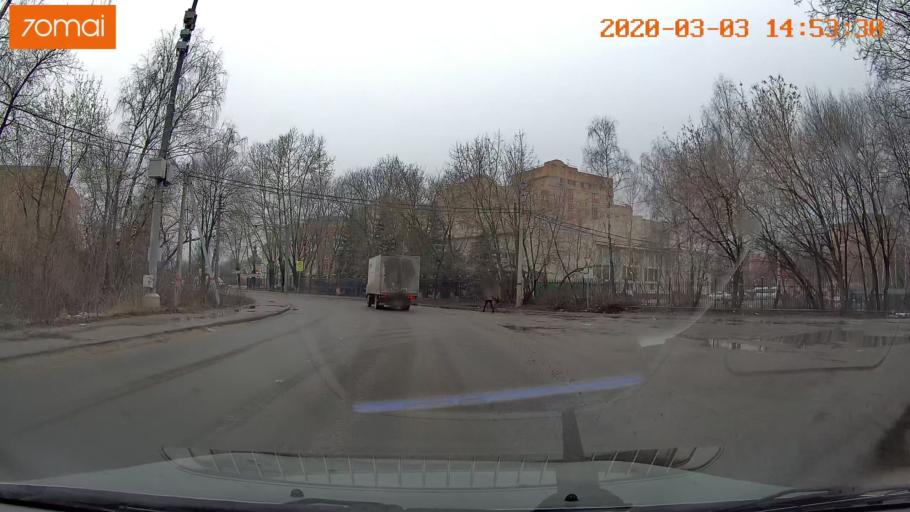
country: RU
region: Moskovskaya
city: Korenevo
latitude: 55.6740
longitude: 38.0083
